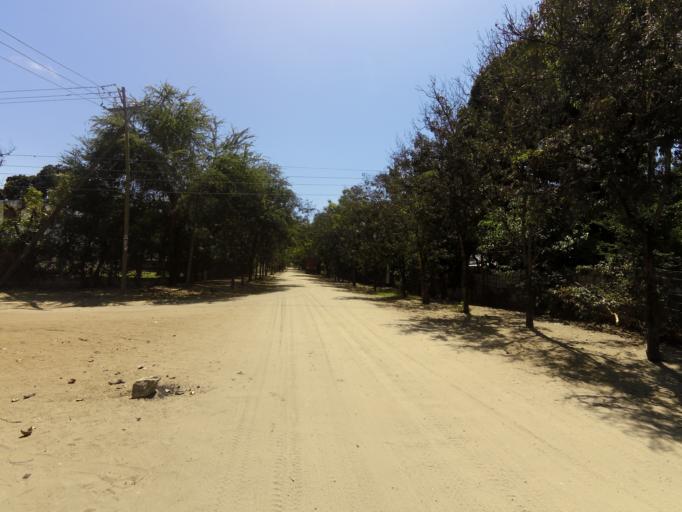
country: TZ
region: Dar es Salaam
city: Magomeni
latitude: -6.7951
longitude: 39.2701
